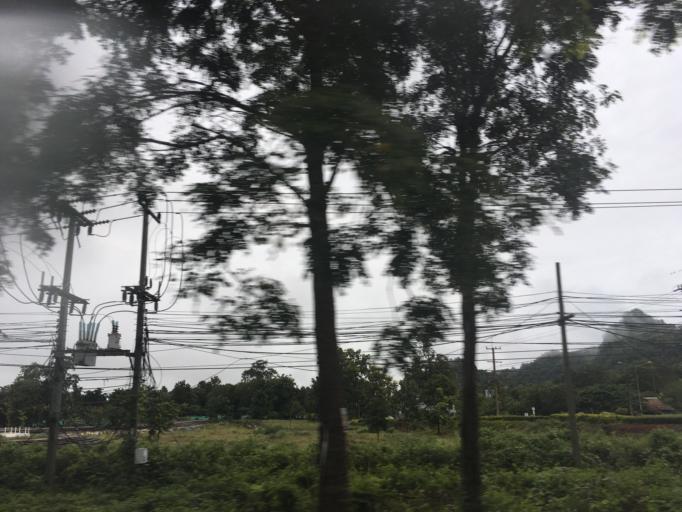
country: TH
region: Kanchanaburi
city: Sai Yok
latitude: 14.1296
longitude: 99.1628
